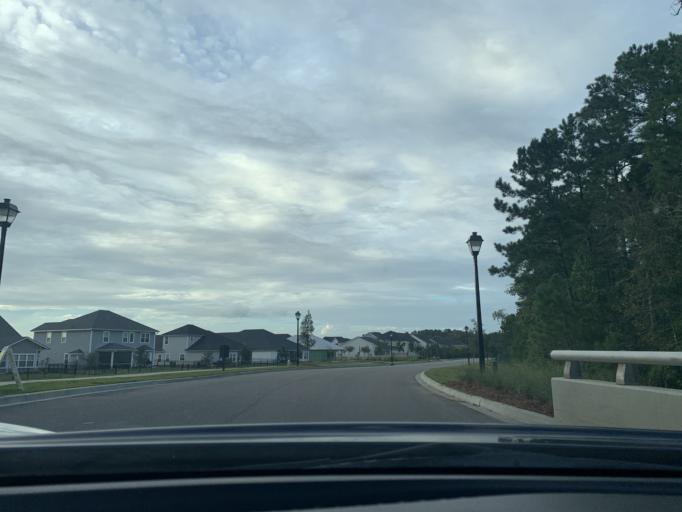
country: US
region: Georgia
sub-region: Chatham County
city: Pooler
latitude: 32.0703
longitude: -81.2577
